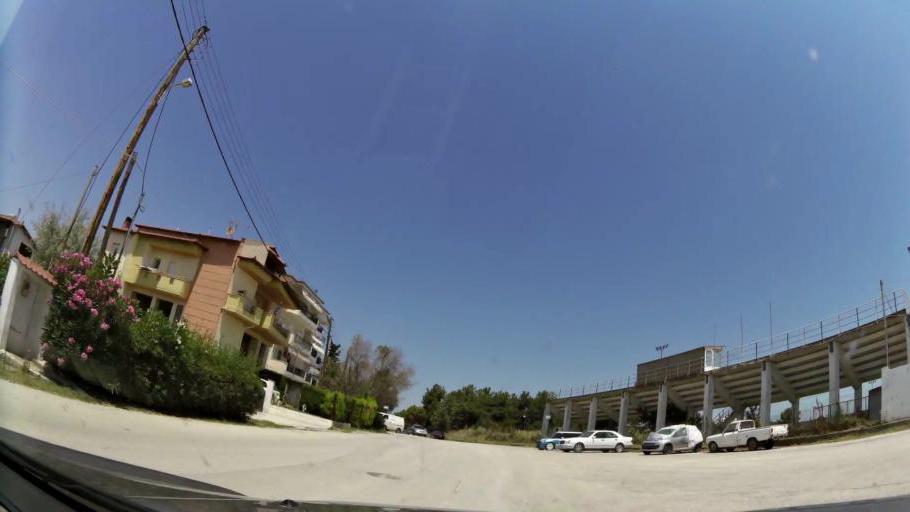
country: GR
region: Central Macedonia
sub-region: Nomos Thessalonikis
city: Epanomi
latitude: 40.4249
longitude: 22.9349
